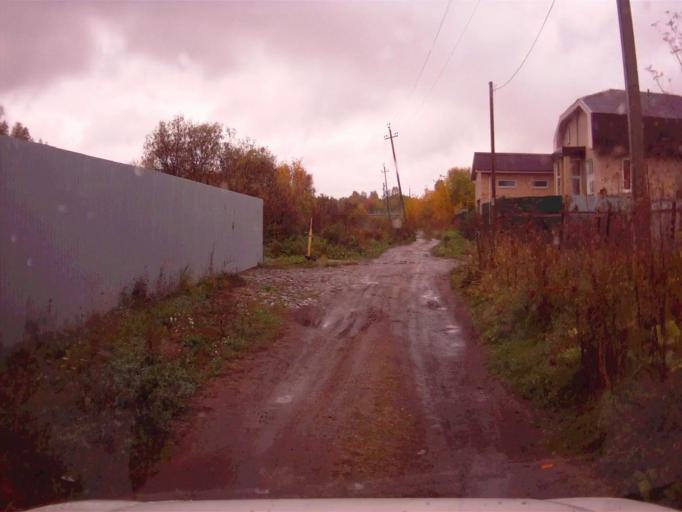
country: RU
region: Chelyabinsk
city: Dolgoderevenskoye
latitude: 55.3014
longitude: 61.3394
